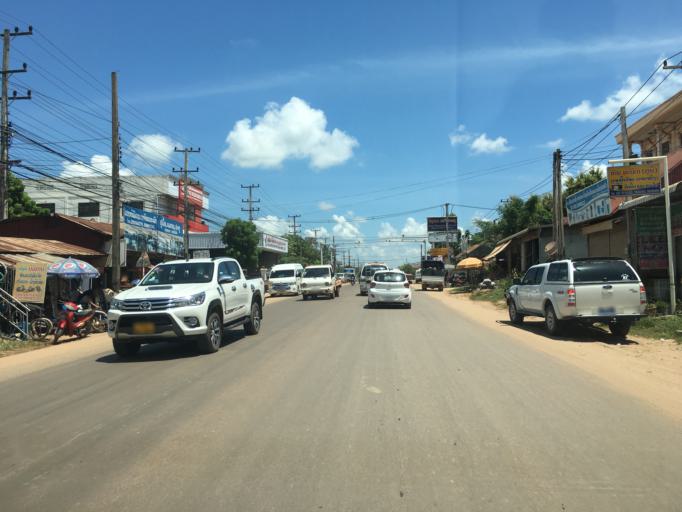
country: TH
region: Nong Khai
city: Si Chiang Mai
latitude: 18.0133
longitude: 102.5459
